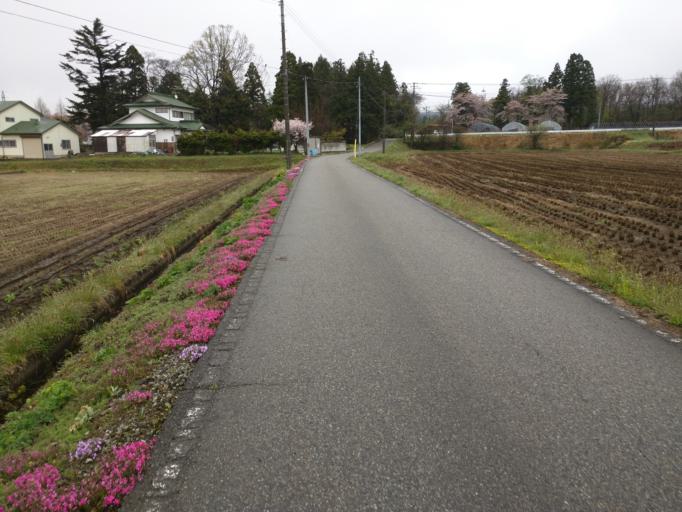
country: JP
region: Fukushima
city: Kitakata
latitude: 37.5396
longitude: 139.9640
